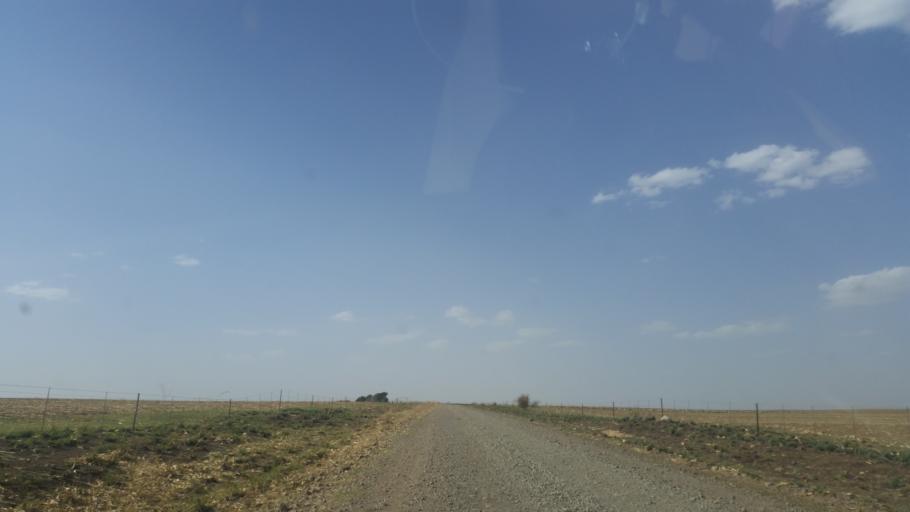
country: ZA
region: Orange Free State
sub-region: Thabo Mofutsanyana District Municipality
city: Phuthaditjhaba
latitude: -28.2344
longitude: 28.6719
